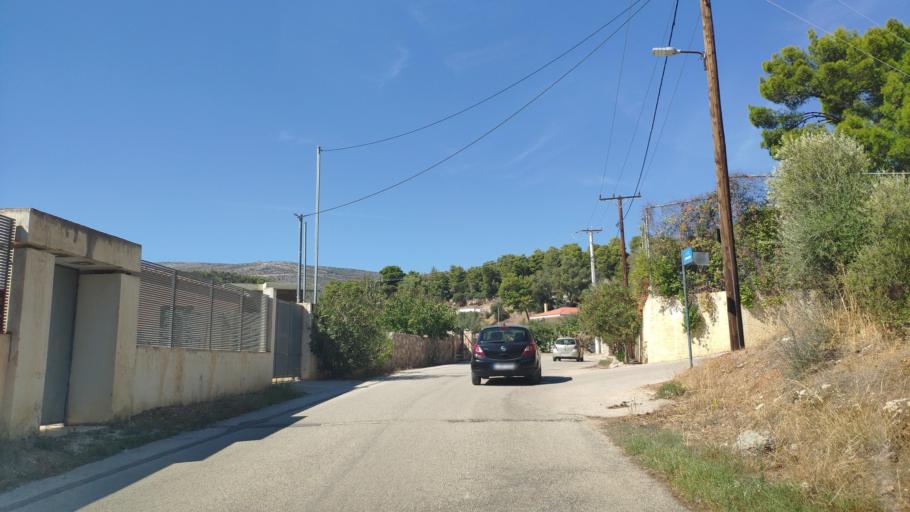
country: GR
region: Attica
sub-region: Nomarchia Anatolikis Attikis
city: Kouvaras
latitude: 37.8400
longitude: 24.0048
